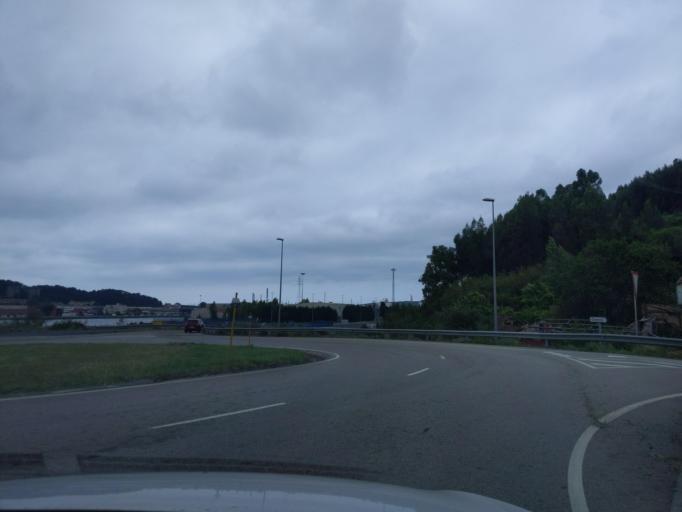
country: ES
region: Asturias
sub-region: Province of Asturias
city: Aviles
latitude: 43.5640
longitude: -5.9151
